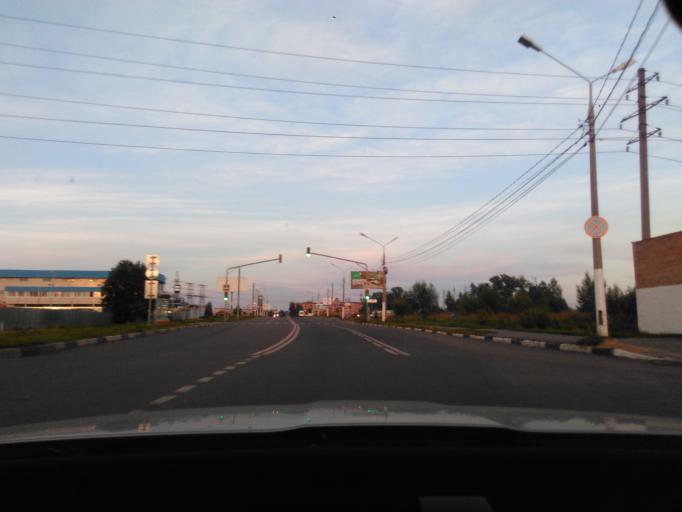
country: RU
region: Moskovskaya
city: Klin
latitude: 56.3172
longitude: 36.7426
